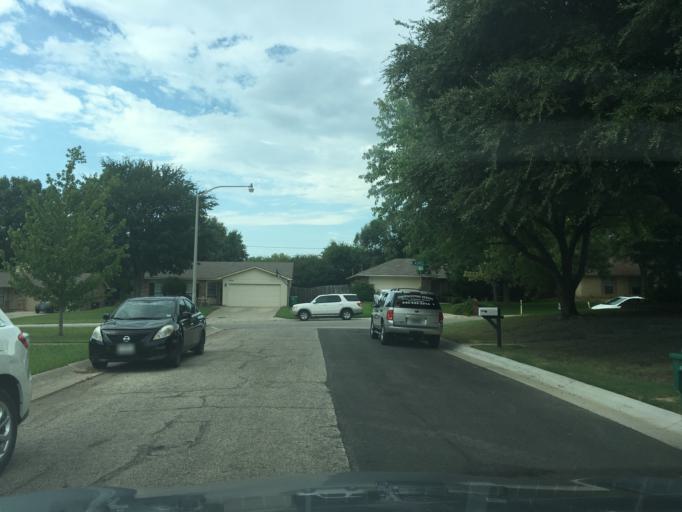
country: US
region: Texas
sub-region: Denton County
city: Denton
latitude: 33.1936
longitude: -97.1581
